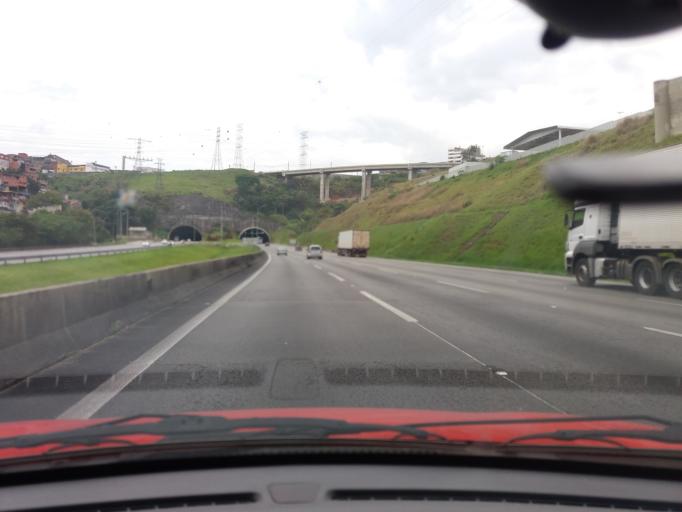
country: BR
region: Sao Paulo
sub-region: Carapicuiba
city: Carapicuiba
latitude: -23.4915
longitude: -46.8093
